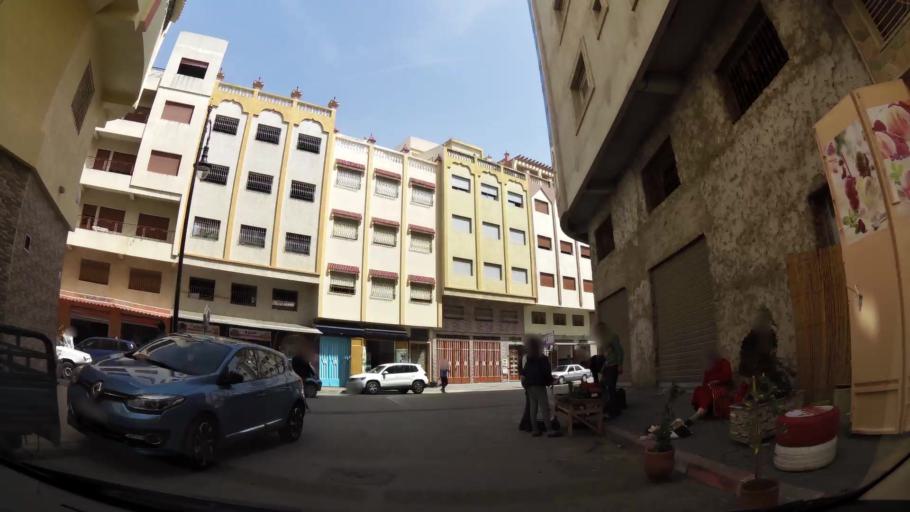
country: MA
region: Tanger-Tetouan
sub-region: Tanger-Assilah
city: Tangier
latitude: 35.7478
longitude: -5.8378
